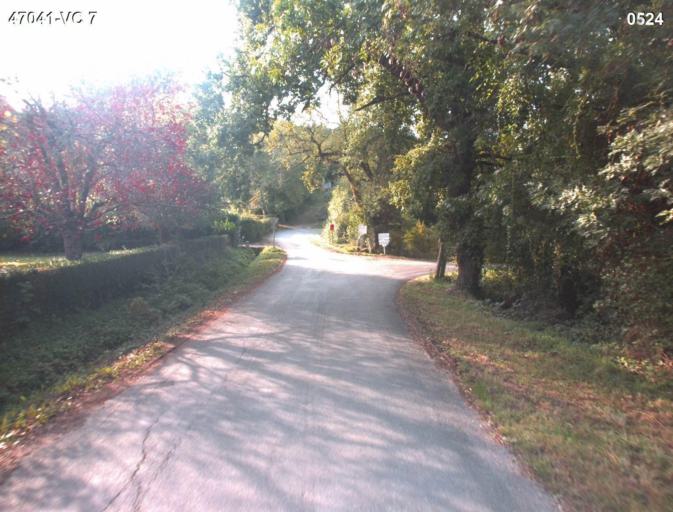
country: FR
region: Aquitaine
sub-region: Departement du Lot-et-Garonne
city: Port-Sainte-Marie
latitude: 44.2011
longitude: 0.4140
